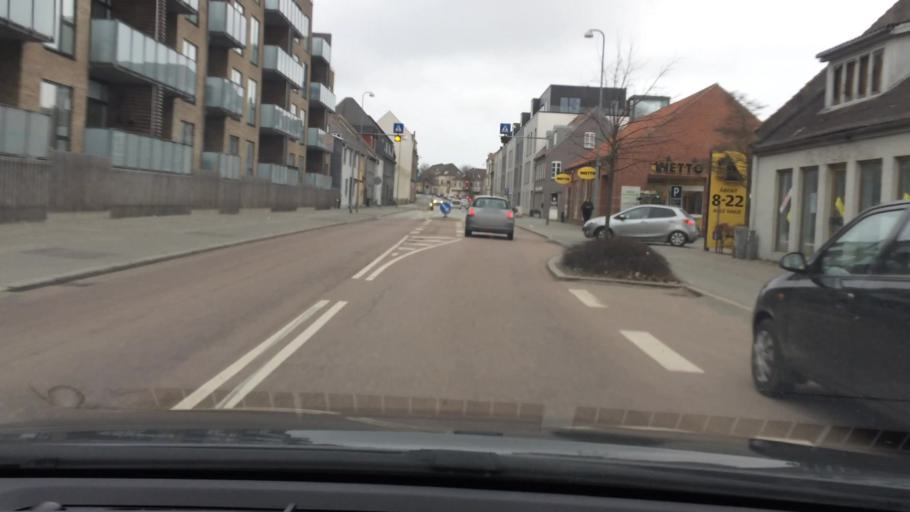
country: DK
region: Central Jutland
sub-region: Horsens Kommune
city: Horsens
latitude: 55.8702
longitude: 9.8408
